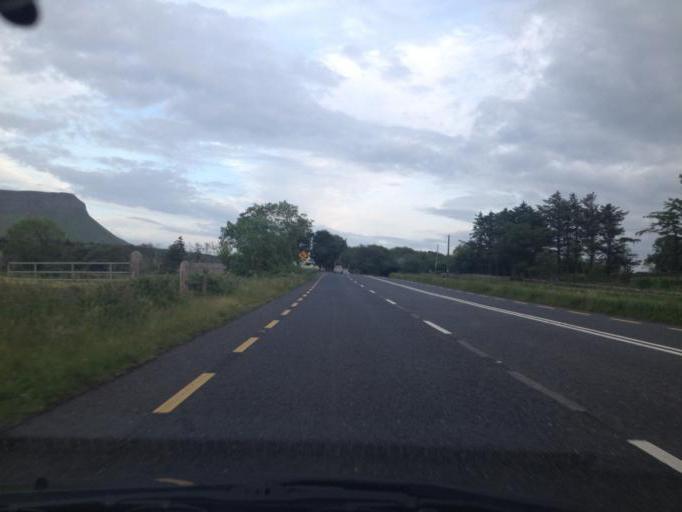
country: IE
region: Connaught
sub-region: Sligo
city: Strandhill
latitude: 54.3844
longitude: -8.5302
